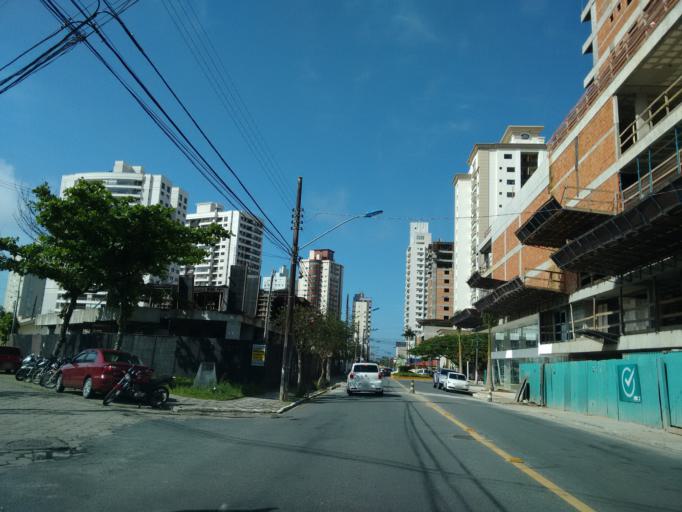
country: BR
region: Santa Catarina
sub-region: Itajai
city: Itajai
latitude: -26.9229
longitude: -48.6519
